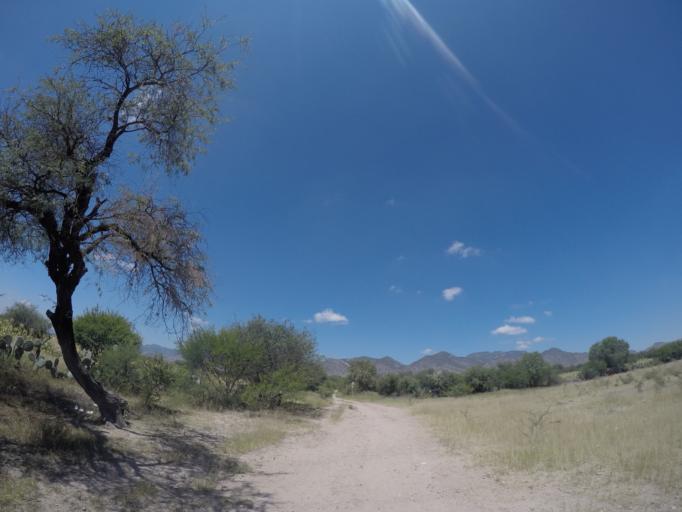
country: MX
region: San Luis Potosi
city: La Pila
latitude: 21.9822
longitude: -100.8949
